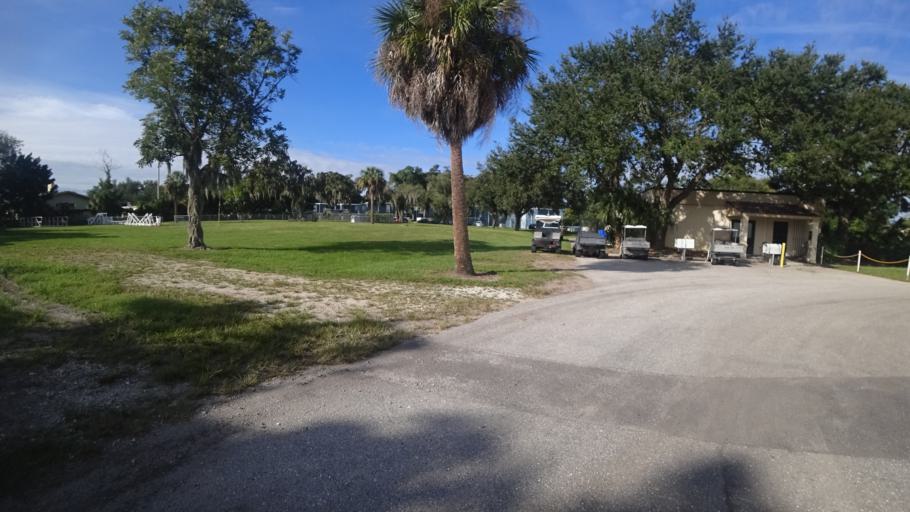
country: US
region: Florida
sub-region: Manatee County
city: West Samoset
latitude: 27.4823
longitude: -82.5643
